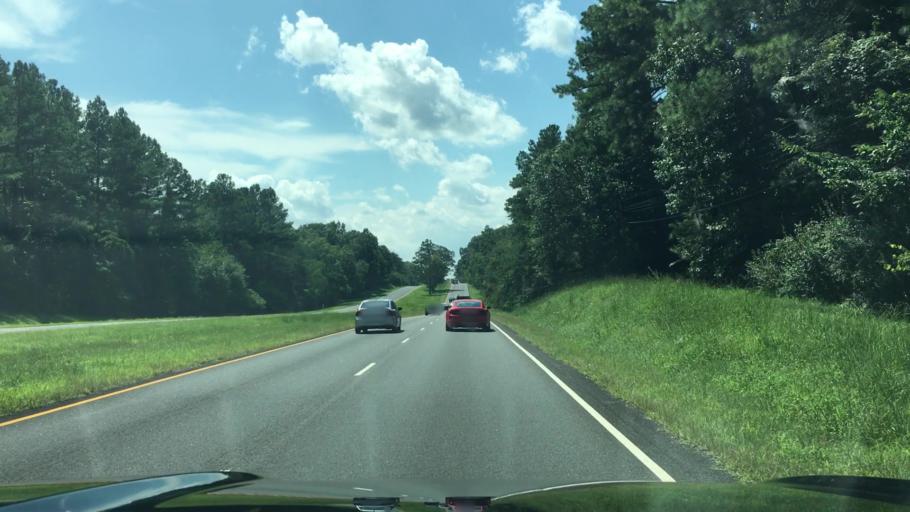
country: US
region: Virginia
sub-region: Prince William County
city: Gainesville
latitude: 38.8051
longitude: -77.5777
